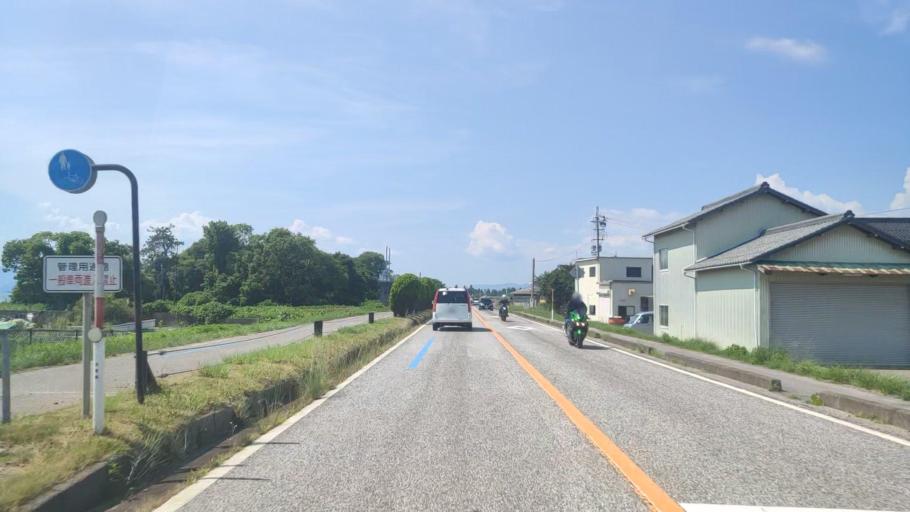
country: JP
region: Shiga Prefecture
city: Nagahama
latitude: 35.4025
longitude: 136.2155
